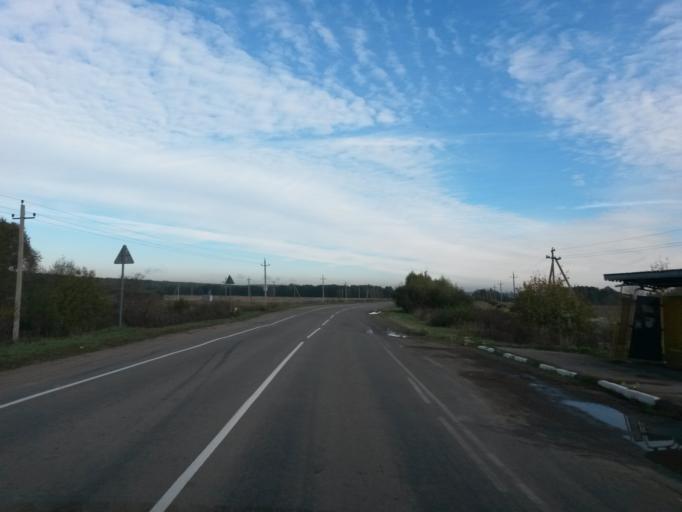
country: RU
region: Moskovskaya
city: Barybino
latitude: 55.2161
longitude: 37.7862
